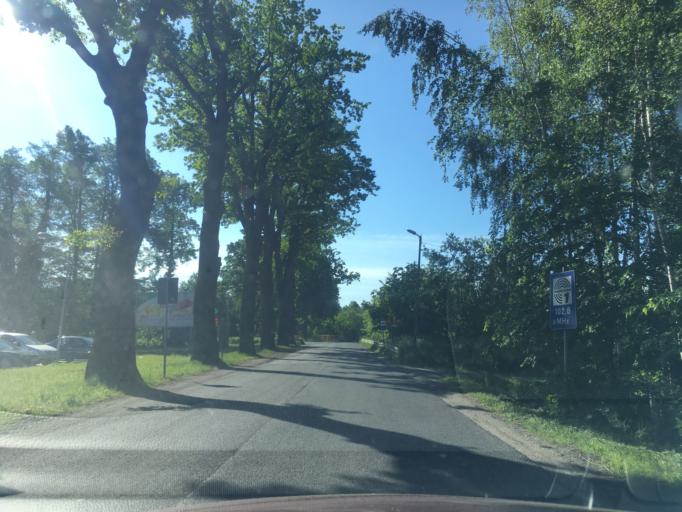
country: PL
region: Lower Silesian Voivodeship
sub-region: Powiat zgorzelecki
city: Sulikow
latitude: 51.0798
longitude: 15.0575
